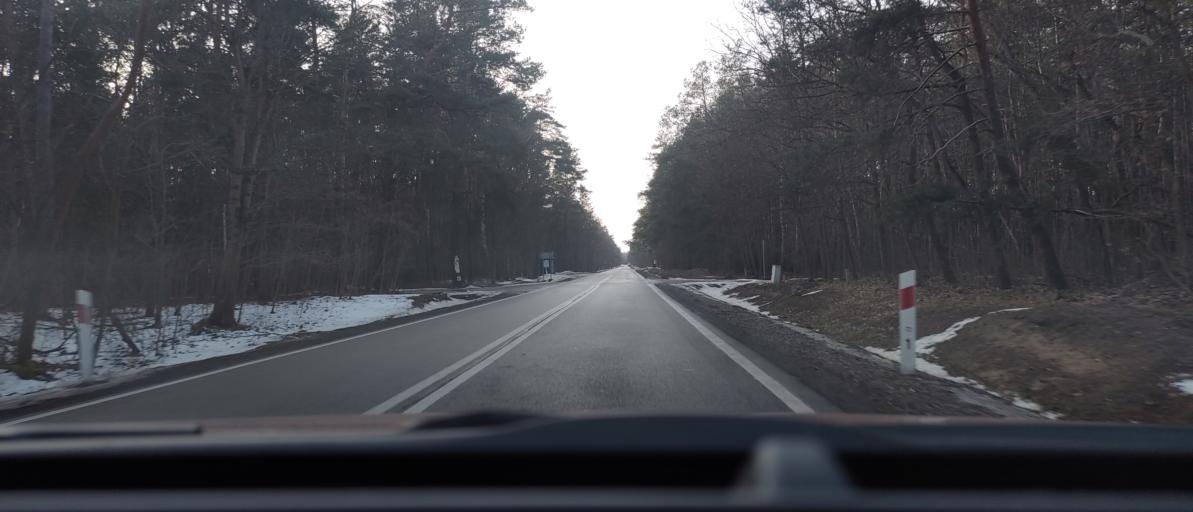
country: PL
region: Masovian Voivodeship
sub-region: Powiat bialobrzeski
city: Wysmierzyce
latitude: 51.6271
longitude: 20.8566
